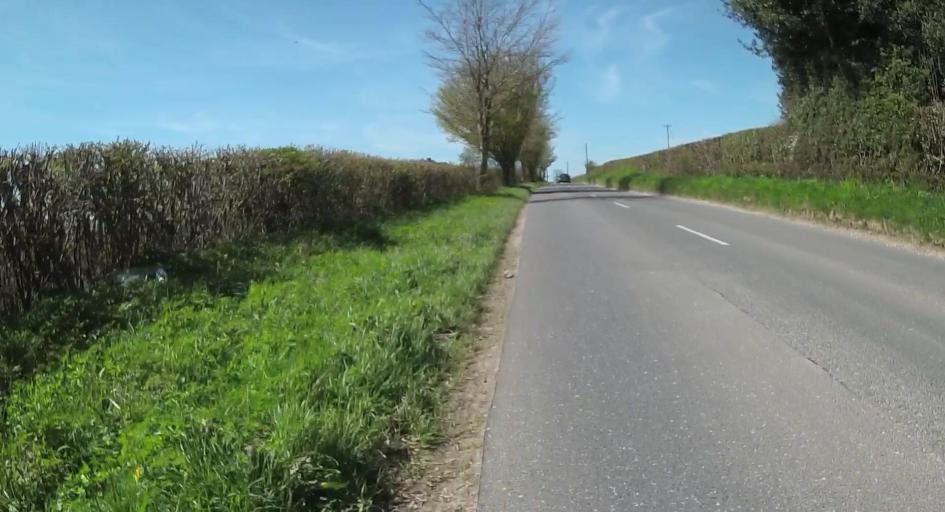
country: GB
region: England
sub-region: Hampshire
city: Winchester
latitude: 51.1020
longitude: -1.3683
